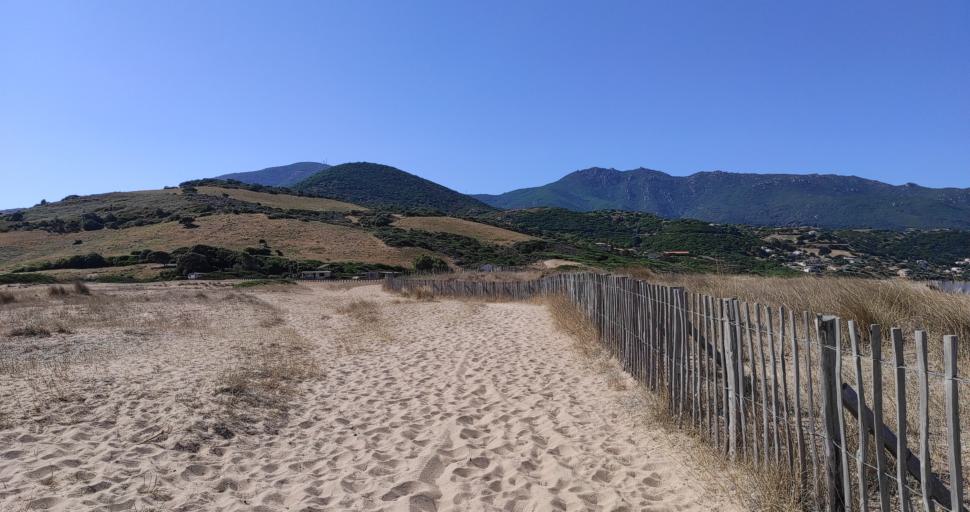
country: FR
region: Corsica
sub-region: Departement de la Corse-du-Sud
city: Alata
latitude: 41.9903
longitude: 8.6701
